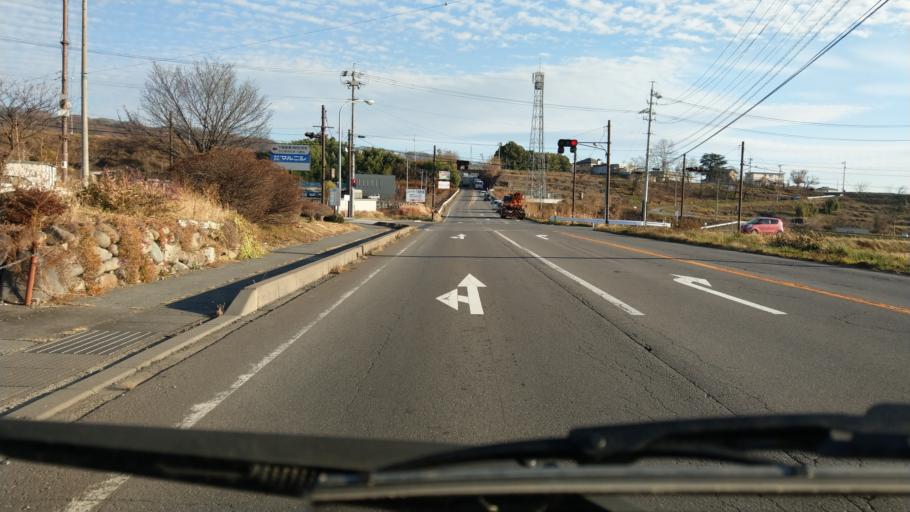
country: JP
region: Nagano
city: Ueda
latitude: 36.3955
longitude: 138.2979
